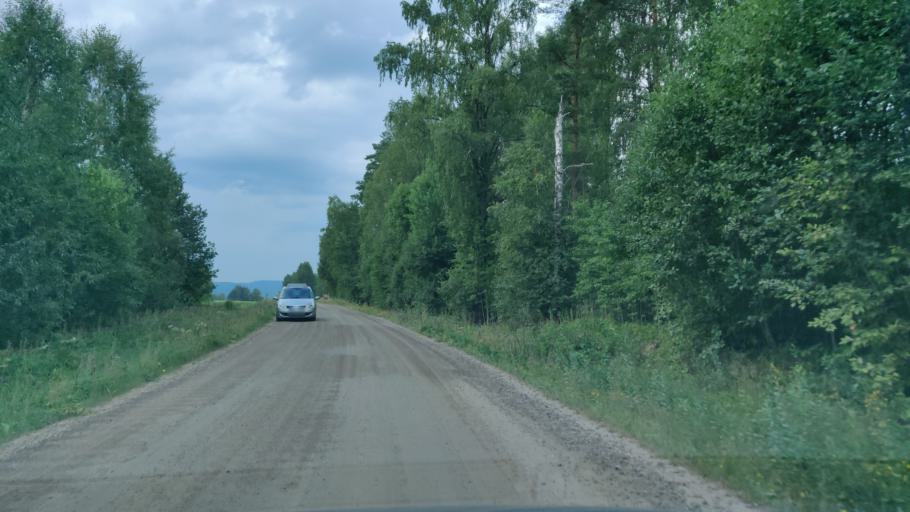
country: SE
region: Vaermland
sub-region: Munkfors Kommun
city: Munkfors
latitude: 59.9625
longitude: 13.4928
